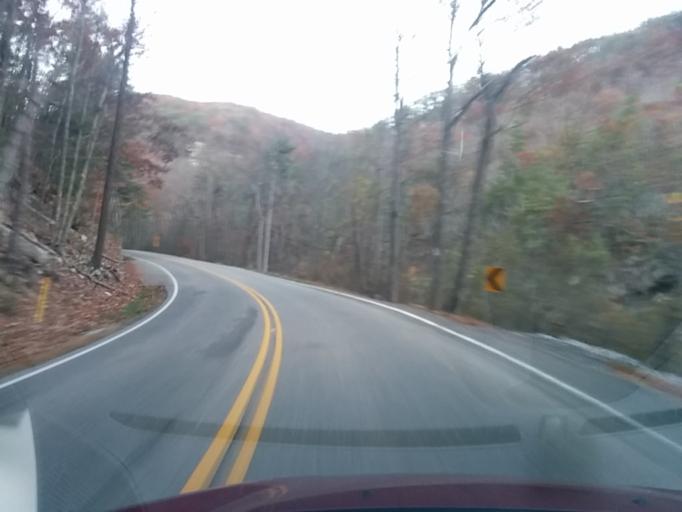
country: US
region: Virginia
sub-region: Rockbridge County
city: East Lexington
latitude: 37.9383
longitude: -79.4519
